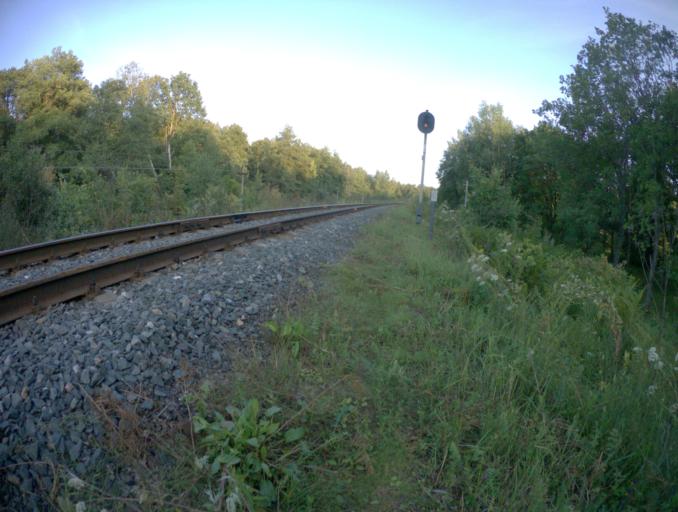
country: RU
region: Vladimir
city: Raduzhnyy
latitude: 56.0448
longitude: 40.3832
